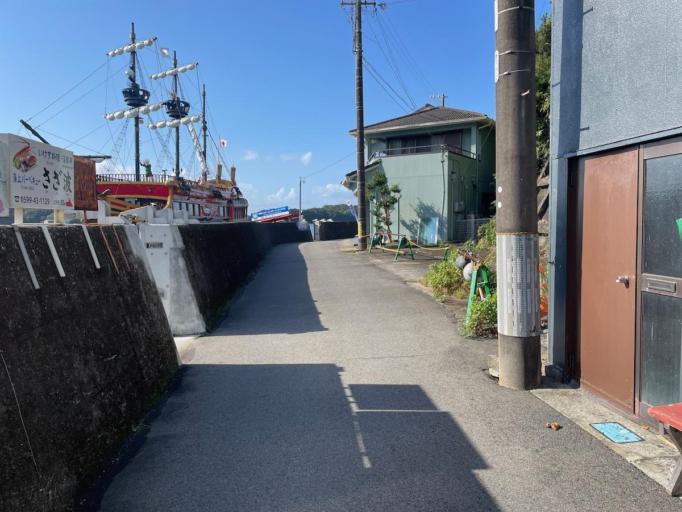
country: JP
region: Mie
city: Toba
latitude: 34.3069
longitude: 136.8187
